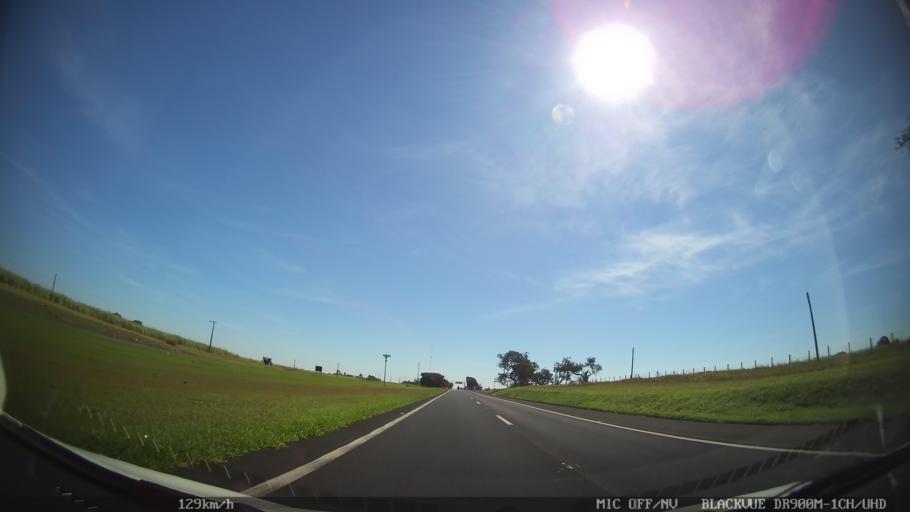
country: BR
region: Sao Paulo
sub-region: Santa Rita Do Passa Quatro
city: Santa Rita do Passa Quatro
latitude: -21.6879
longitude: -47.6004
